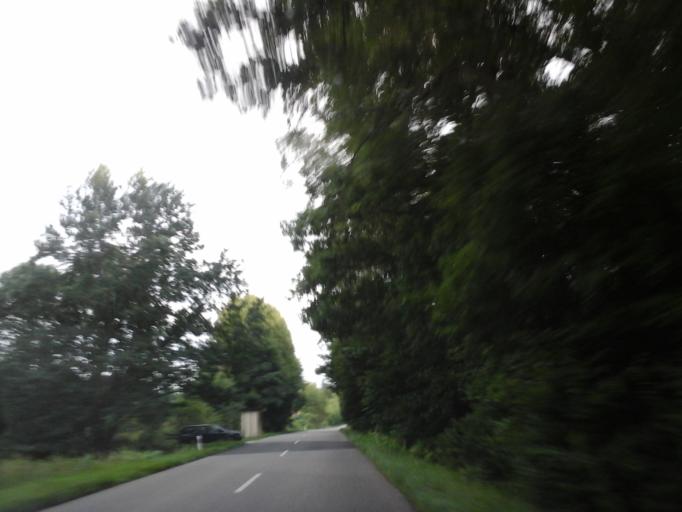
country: PL
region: West Pomeranian Voivodeship
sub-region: Powiat kamienski
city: Golczewo
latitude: 53.7303
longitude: 15.0212
